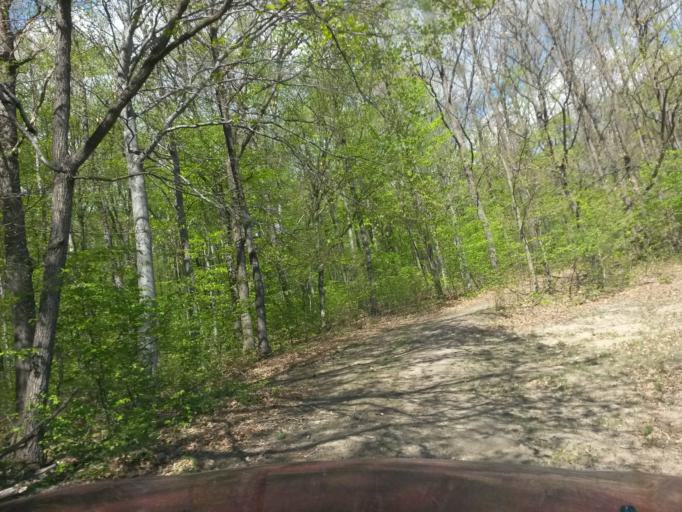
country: SK
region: Presovsky
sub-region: Okres Presov
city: Presov
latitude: 48.9410
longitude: 21.1221
